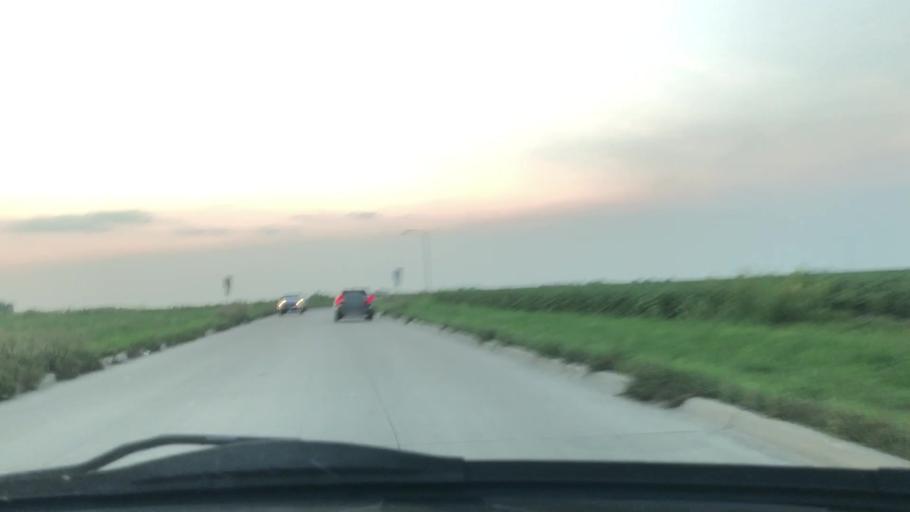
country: US
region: Iowa
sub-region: Johnson County
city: North Liberty
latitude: 41.7163
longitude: -91.6052
